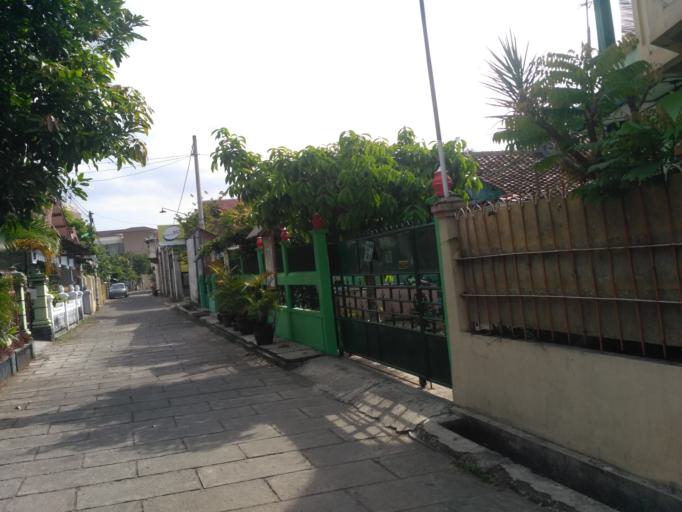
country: ID
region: Daerah Istimewa Yogyakarta
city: Depok
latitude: -7.7807
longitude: 110.4109
